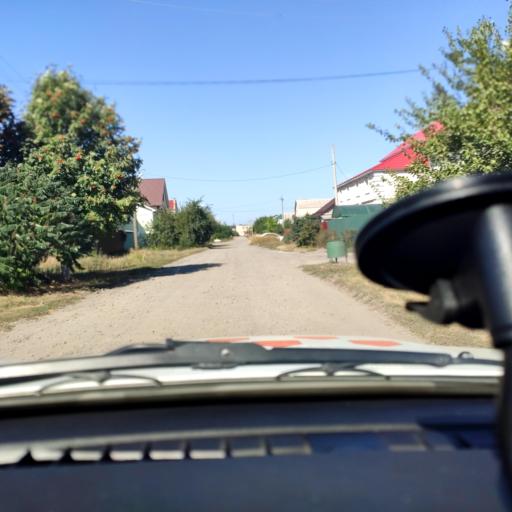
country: RU
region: Voronezj
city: Novaya Usman'
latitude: 51.6079
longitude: 39.3930
